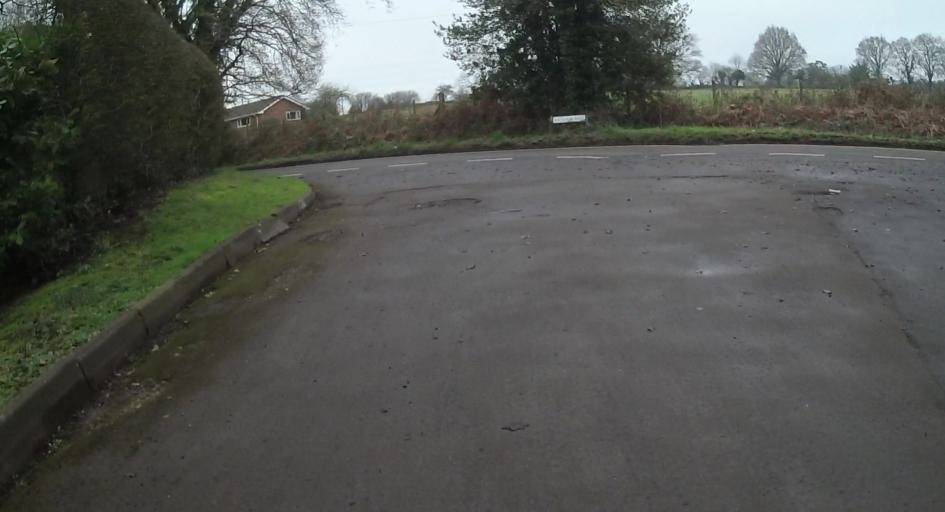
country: GB
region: England
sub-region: Wokingham
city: Barkham
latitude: 51.3944
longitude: -0.8604
